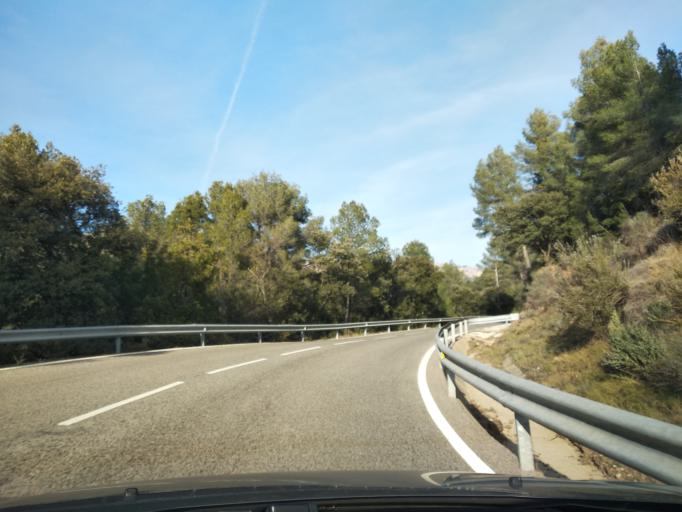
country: ES
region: Catalonia
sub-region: Provincia de Tarragona
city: Margalef
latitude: 41.2376
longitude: 0.7847
